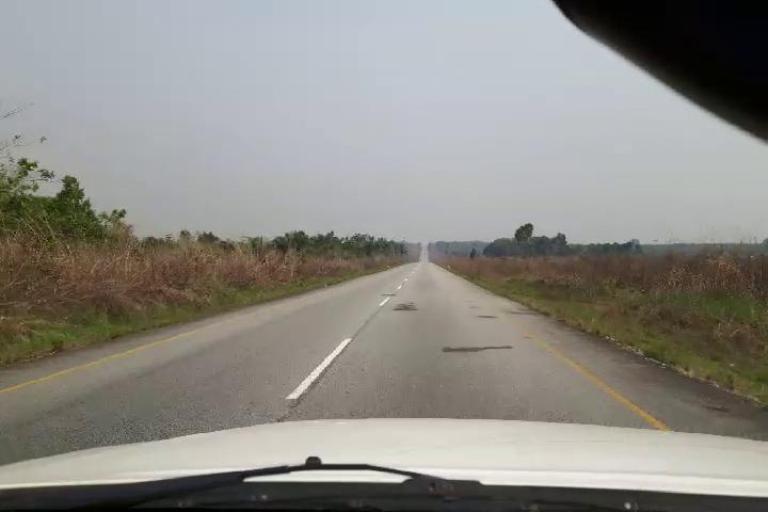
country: SL
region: Southern Province
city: Largo
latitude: 8.2383
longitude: -12.0838
